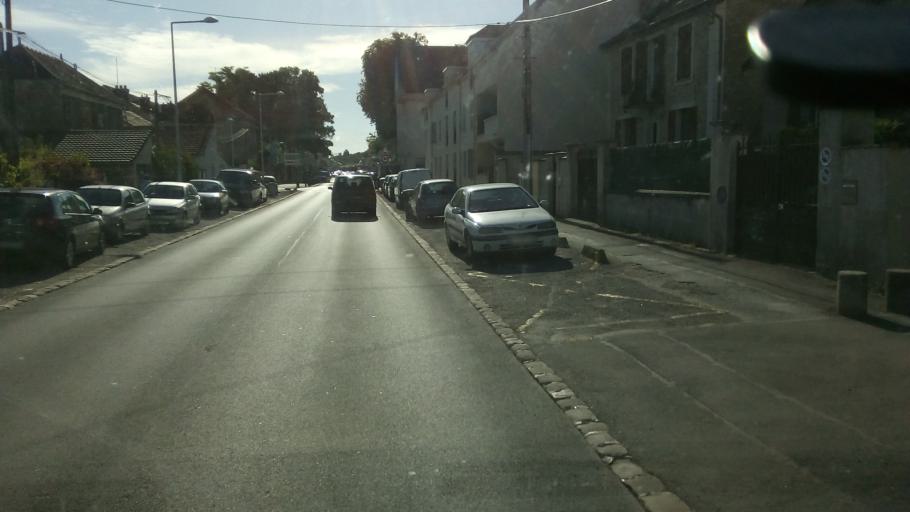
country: FR
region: Ile-de-France
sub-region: Departement de Seine-et-Marne
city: Moissy-Cramayel
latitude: 48.6274
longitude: 2.5874
